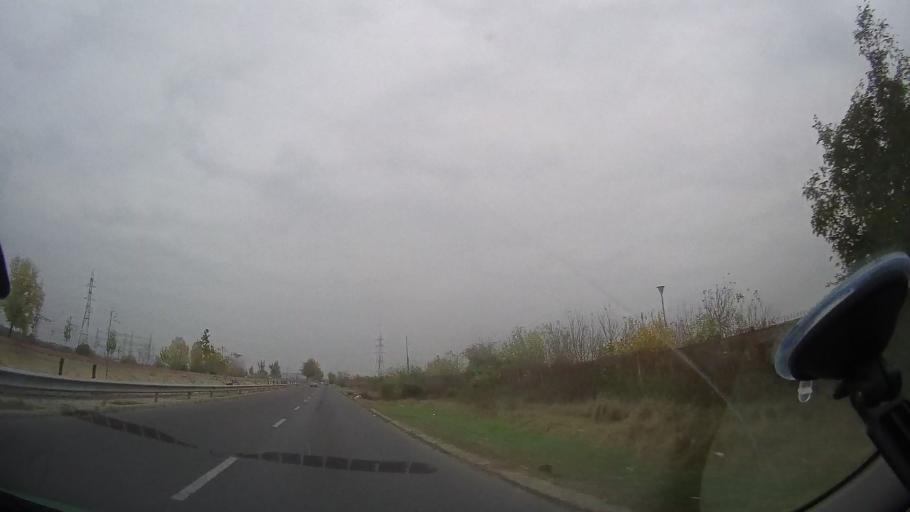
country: RO
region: Ilfov
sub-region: Comuna Popesti-Leordeni
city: Popesti-Leordeni
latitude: 44.3958
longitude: 26.1720
